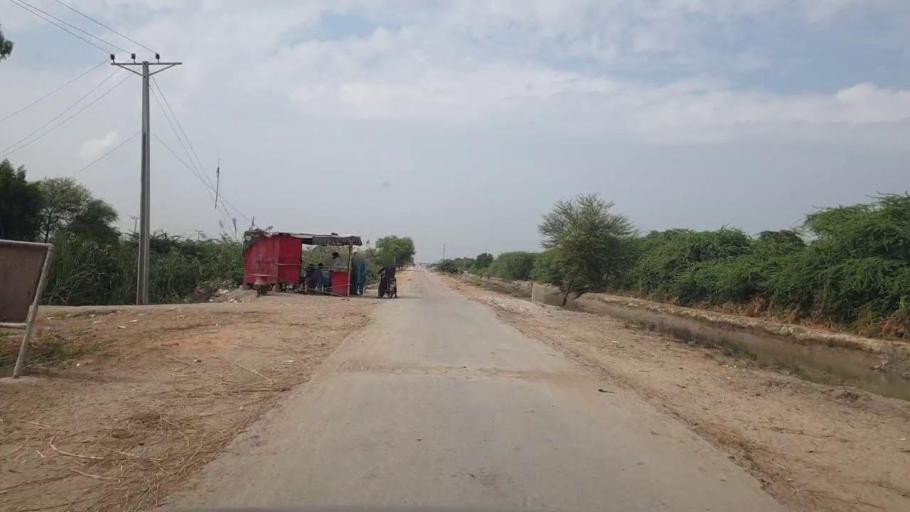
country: PK
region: Sindh
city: Kario
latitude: 24.6317
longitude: 68.5708
